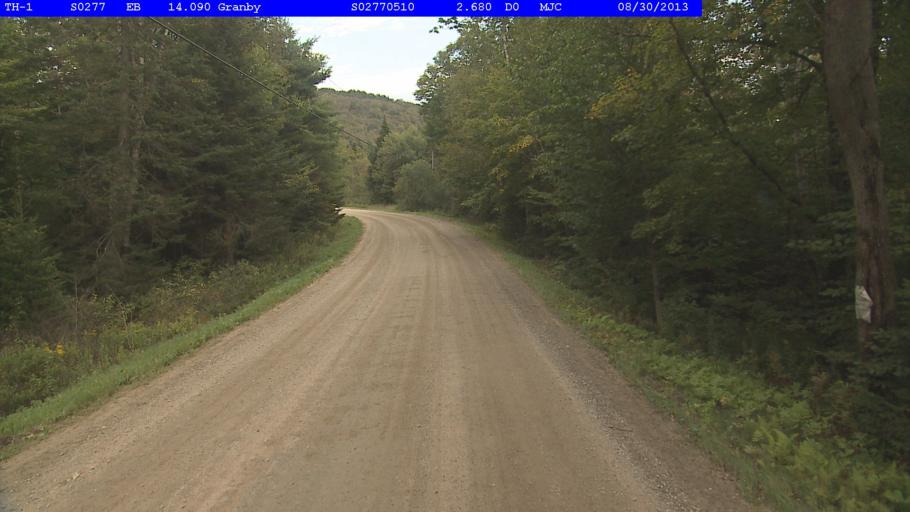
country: US
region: Vermont
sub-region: Essex County
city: Guildhall
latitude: 44.5761
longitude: -71.7140
